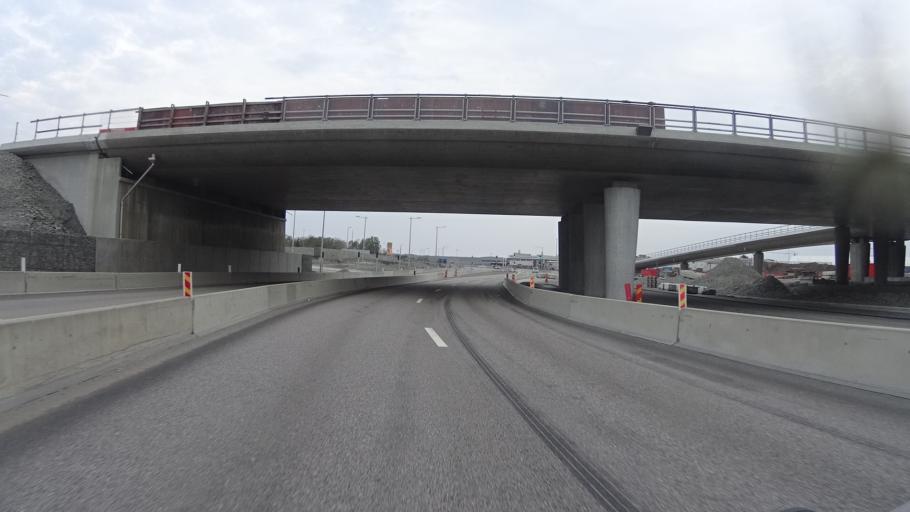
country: SE
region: Vaestra Goetaland
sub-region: Goteborg
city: Torslanda
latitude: 57.7115
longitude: 11.8415
